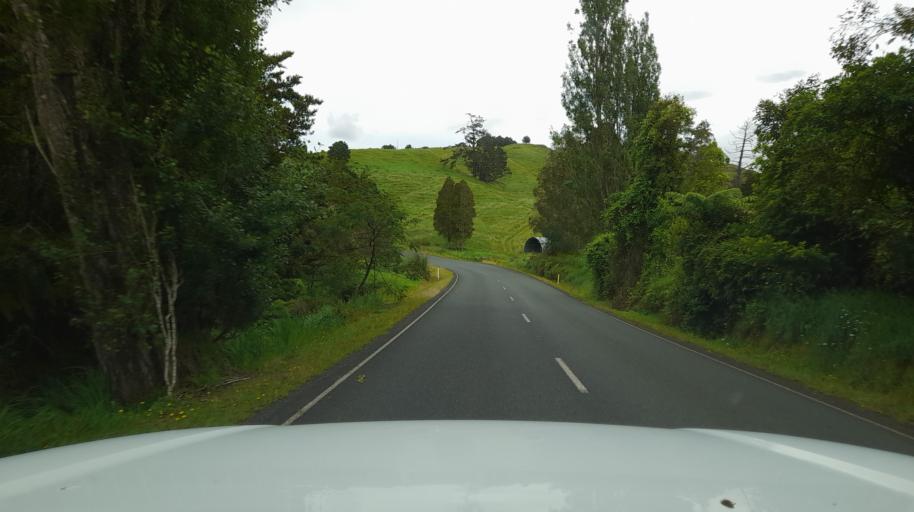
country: NZ
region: Northland
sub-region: Far North District
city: Kaitaia
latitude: -35.2933
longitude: 173.3700
